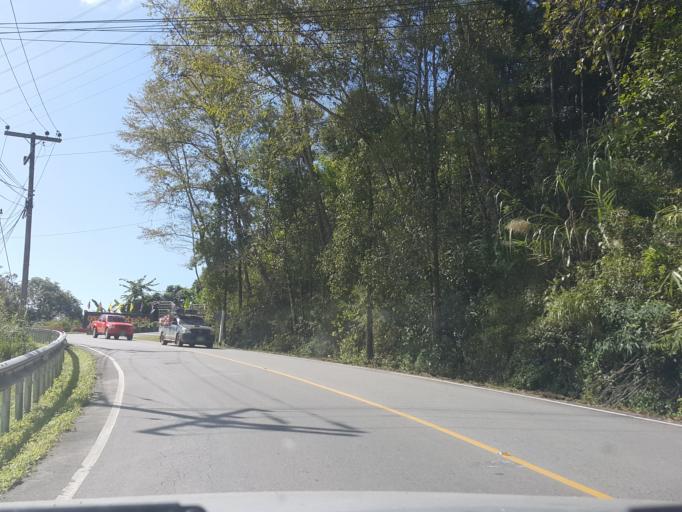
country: TH
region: Mae Hong Son
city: Mae Hi
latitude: 19.2785
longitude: 98.6042
